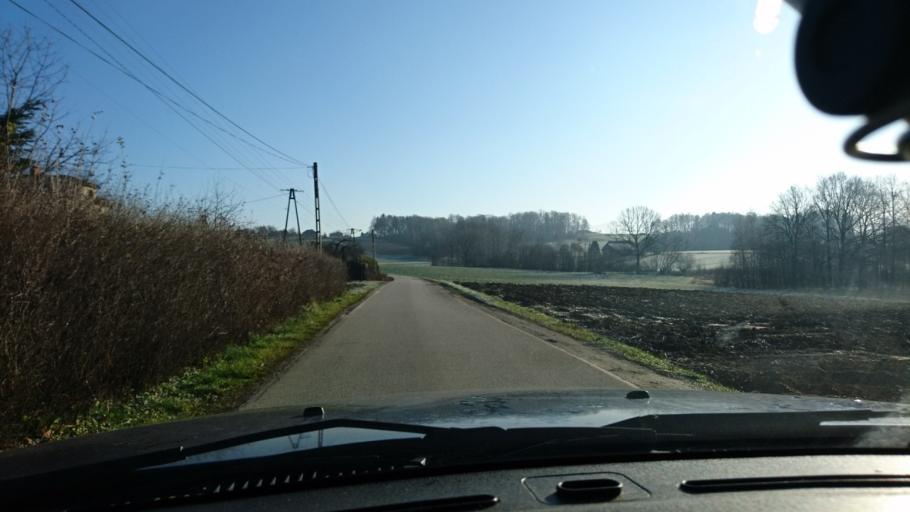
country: PL
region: Silesian Voivodeship
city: Janowice
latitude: 49.8948
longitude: 19.1063
